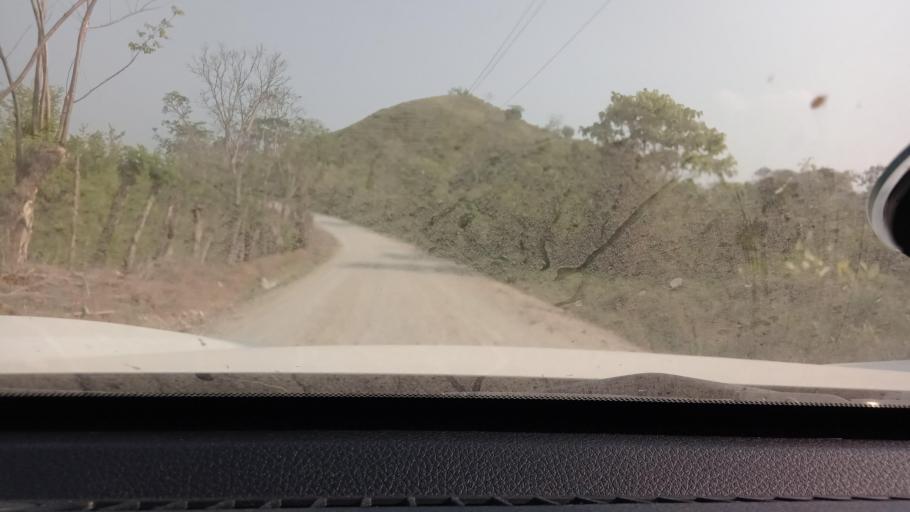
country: MX
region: Tabasco
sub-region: Huimanguillo
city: Francisco Rueda
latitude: 17.6174
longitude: -93.9404
